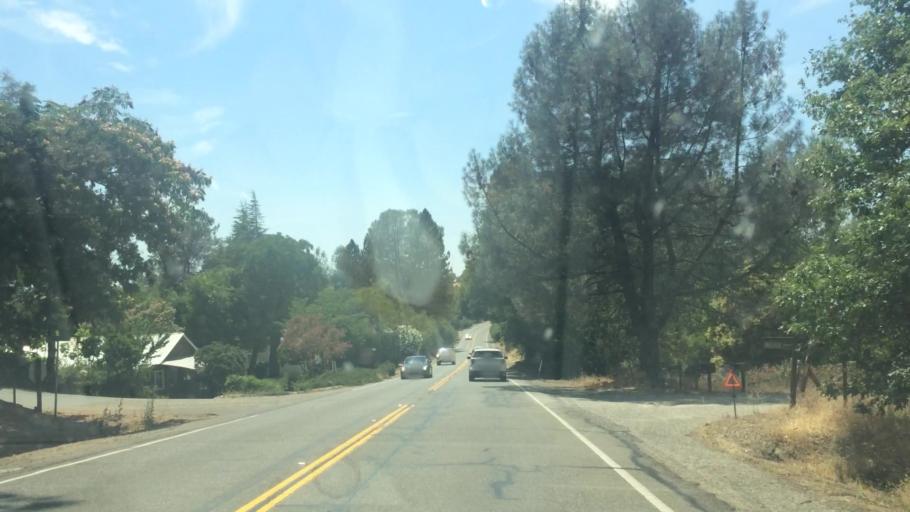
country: US
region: California
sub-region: Amador County
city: Jackson
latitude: 38.3990
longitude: -120.7369
